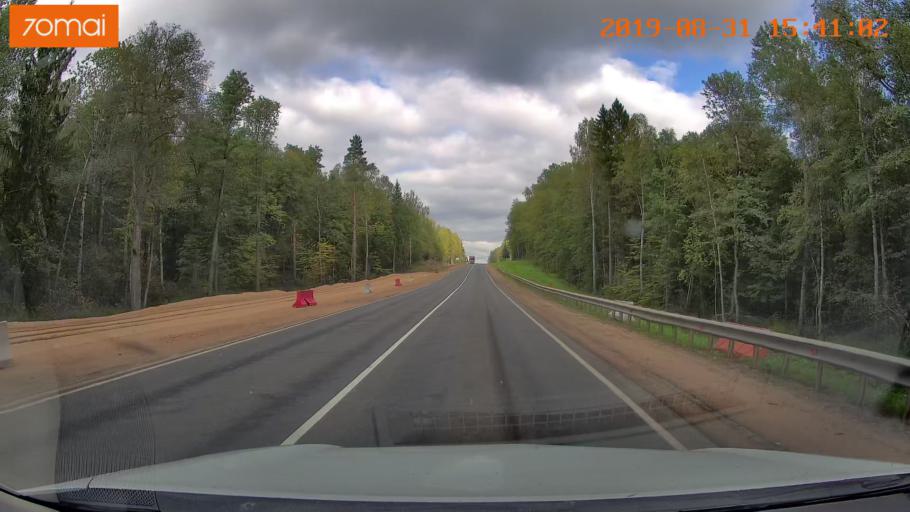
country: RU
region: Kaluga
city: Mosal'sk
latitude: 54.6364
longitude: 34.8503
